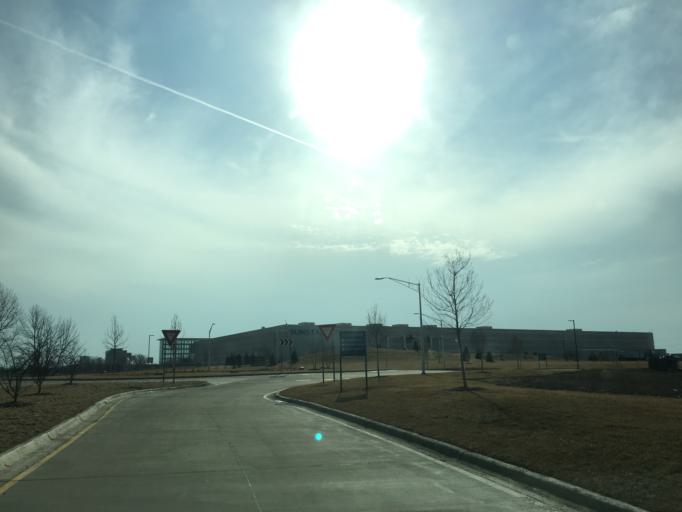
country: US
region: Illinois
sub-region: Cook County
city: Hoffman Estates
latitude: 42.0663
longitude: -88.0726
